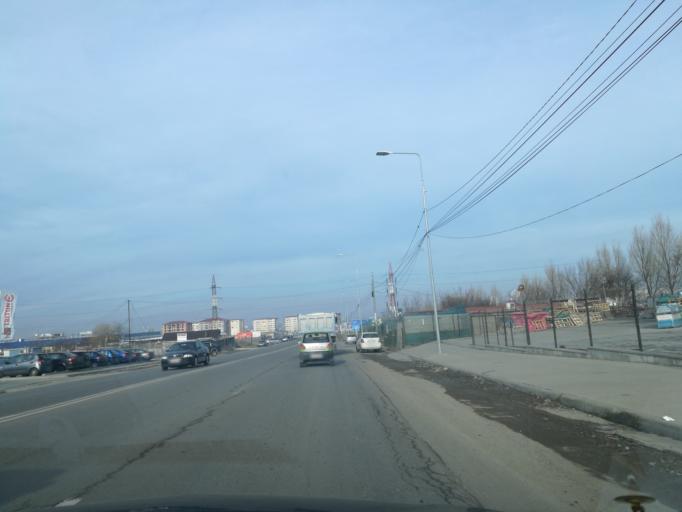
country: RO
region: Constanta
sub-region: Municipiul Constanta
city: Constanta
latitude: 44.1938
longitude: 28.6033
